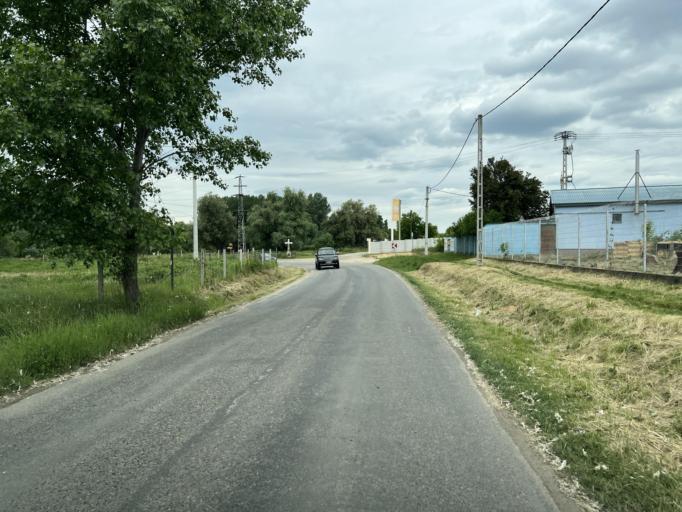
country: HU
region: Pest
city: Nagytarcsa
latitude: 47.5408
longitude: 19.2775
